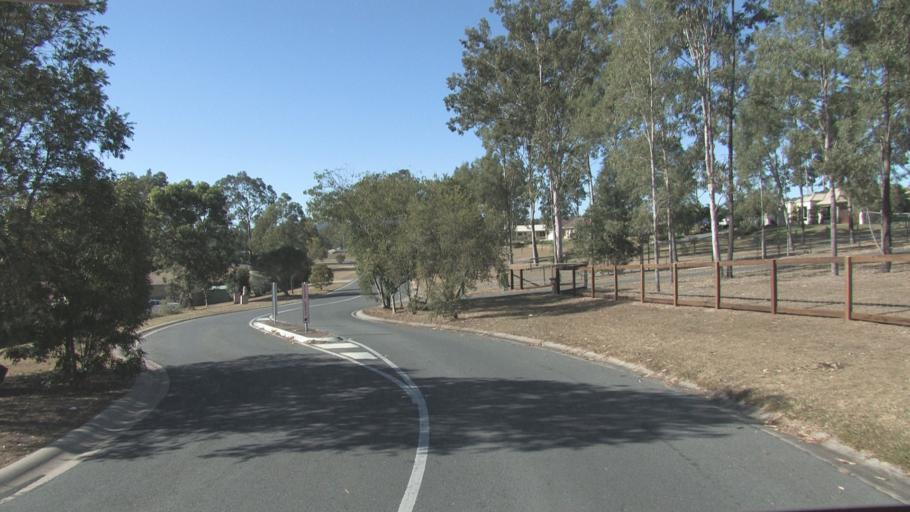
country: AU
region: Queensland
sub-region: Logan
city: Cedar Vale
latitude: -27.8643
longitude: 153.0365
